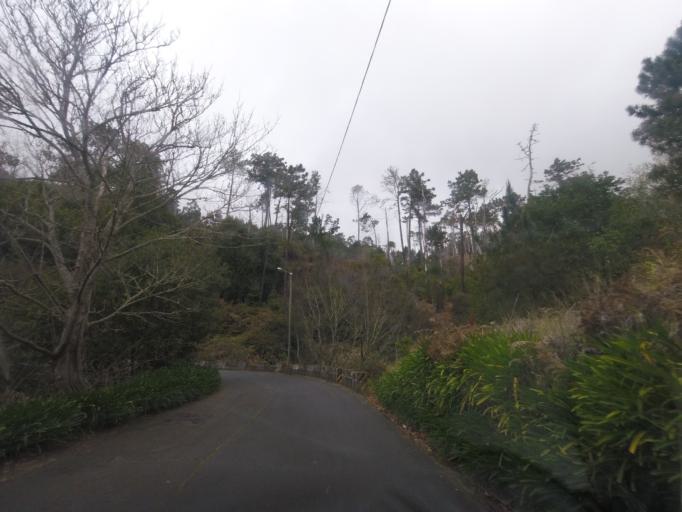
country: PT
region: Madeira
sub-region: Calheta
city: Faja da Ovelha
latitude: 32.7681
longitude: -17.2099
